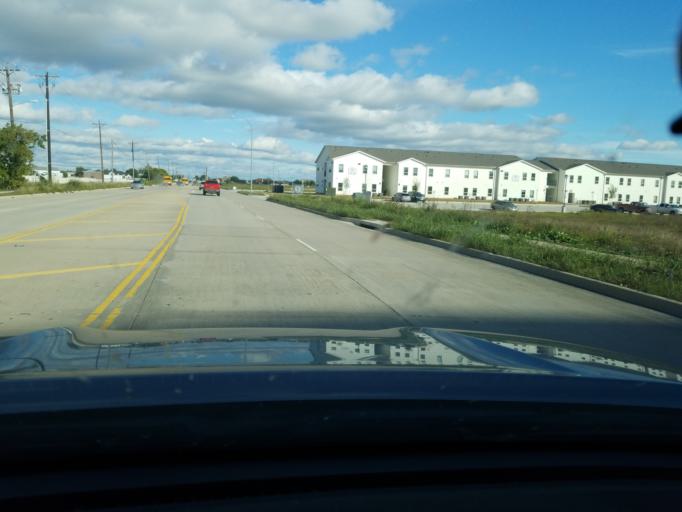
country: US
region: Texas
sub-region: Tarrant County
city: Haslet
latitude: 32.9688
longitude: -97.4098
